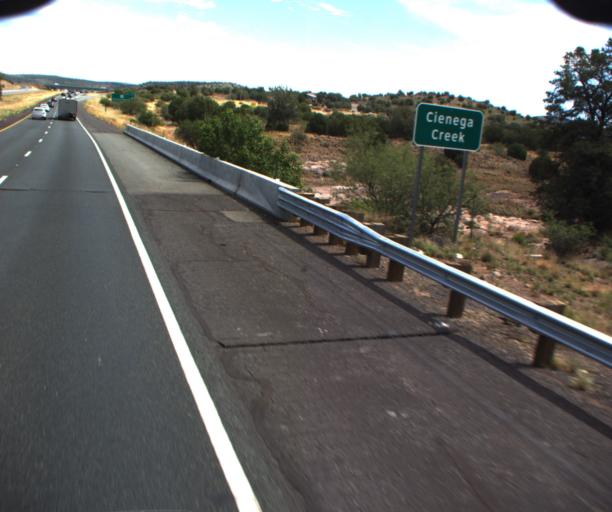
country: US
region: Arizona
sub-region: Yavapai County
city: Camp Verde
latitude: 34.5082
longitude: -111.9964
